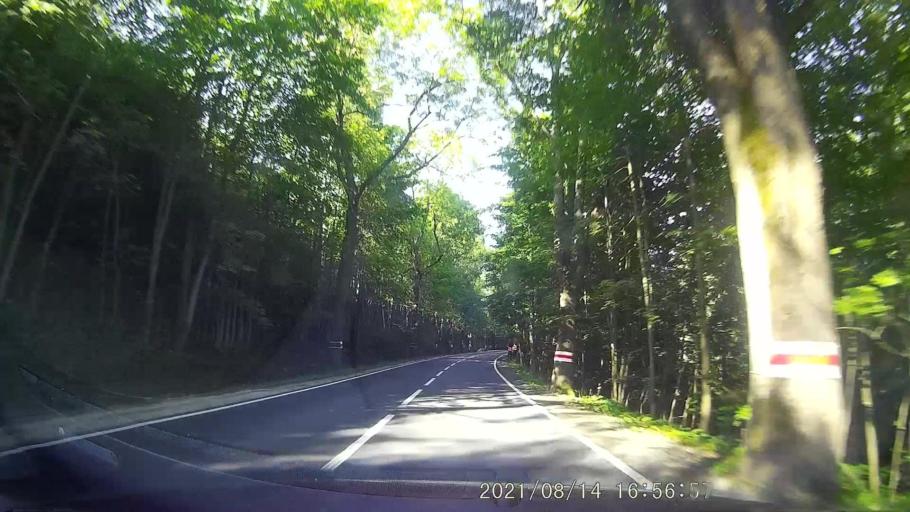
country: PL
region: Lower Silesian Voivodeship
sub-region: Powiat jeleniogorski
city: Kowary
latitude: 50.7571
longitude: 15.8658
